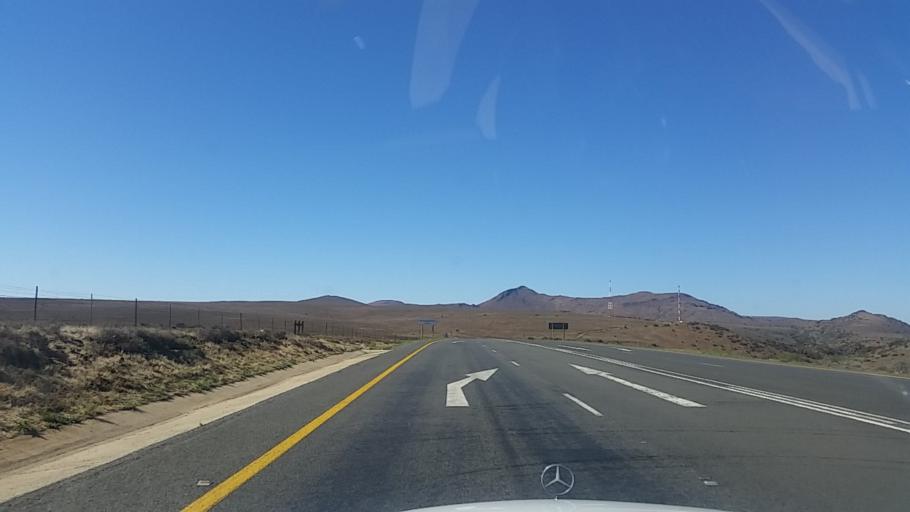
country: ZA
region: Eastern Cape
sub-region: Cacadu District Municipality
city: Graaff-Reinet
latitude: -31.9534
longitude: 24.7265
